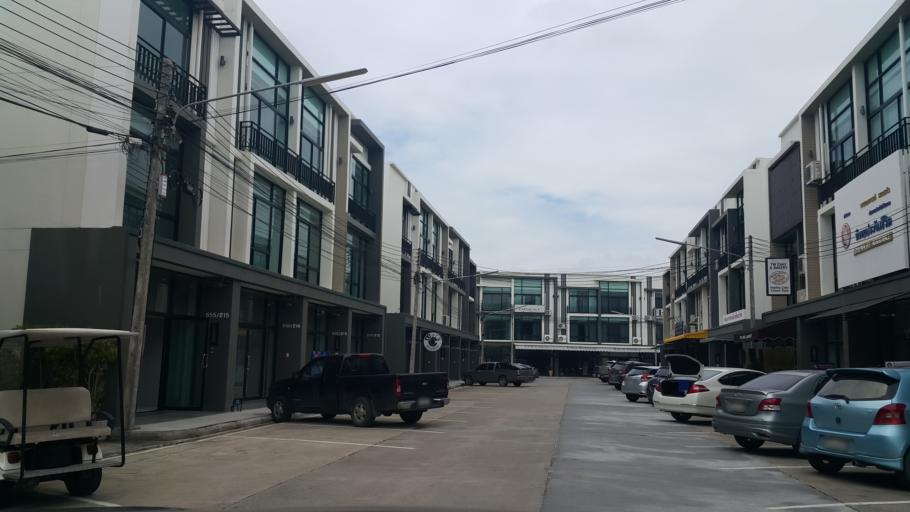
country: TH
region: Chiang Mai
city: San Sai
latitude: 18.8291
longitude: 99.0140
